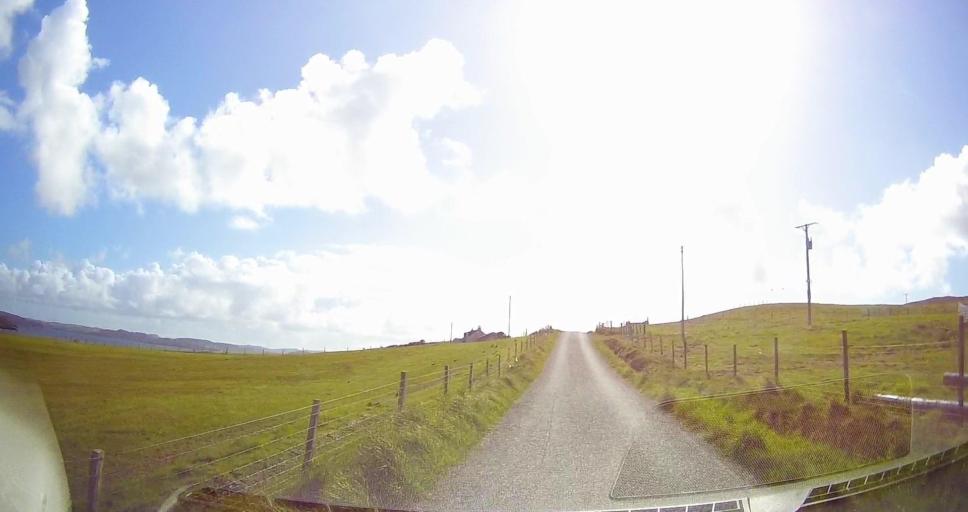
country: GB
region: Scotland
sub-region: Shetland Islands
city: Lerwick
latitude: 60.3535
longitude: -1.3937
